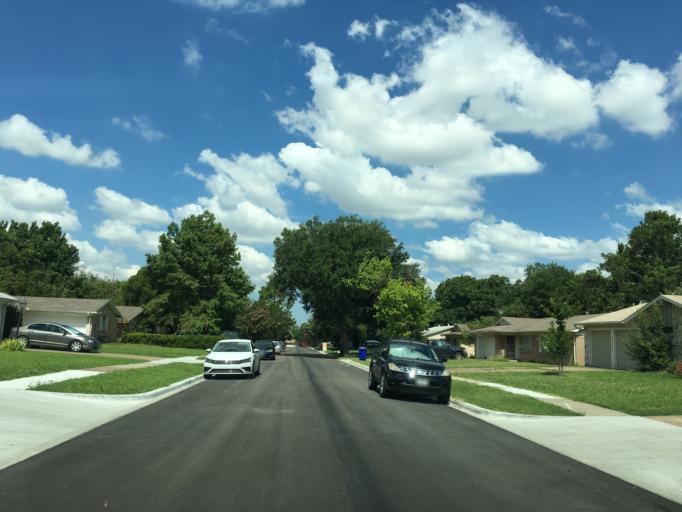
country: US
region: Texas
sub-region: Dallas County
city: Farmers Branch
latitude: 32.9291
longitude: -96.8758
